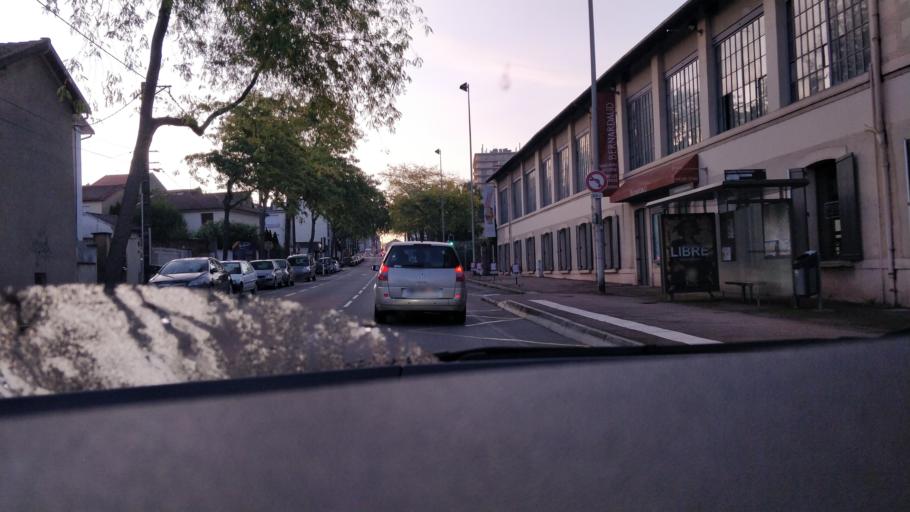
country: FR
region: Limousin
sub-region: Departement de la Haute-Vienne
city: Limoges
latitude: 45.8353
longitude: 1.2446
